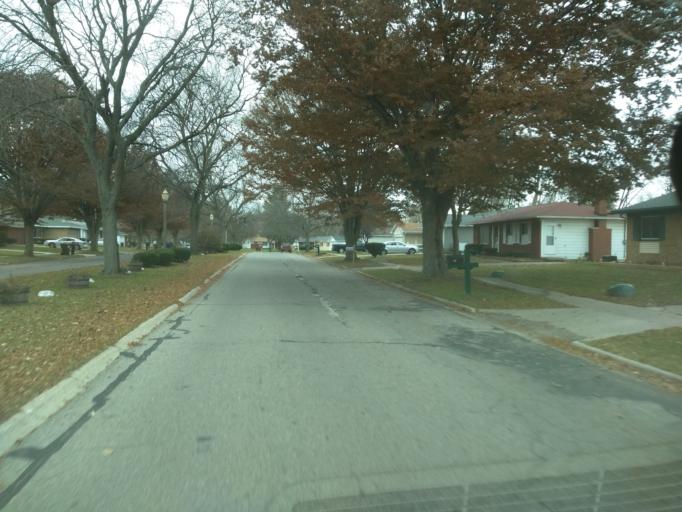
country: US
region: Michigan
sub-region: Eaton County
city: Waverly
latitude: 42.6940
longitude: -84.6037
